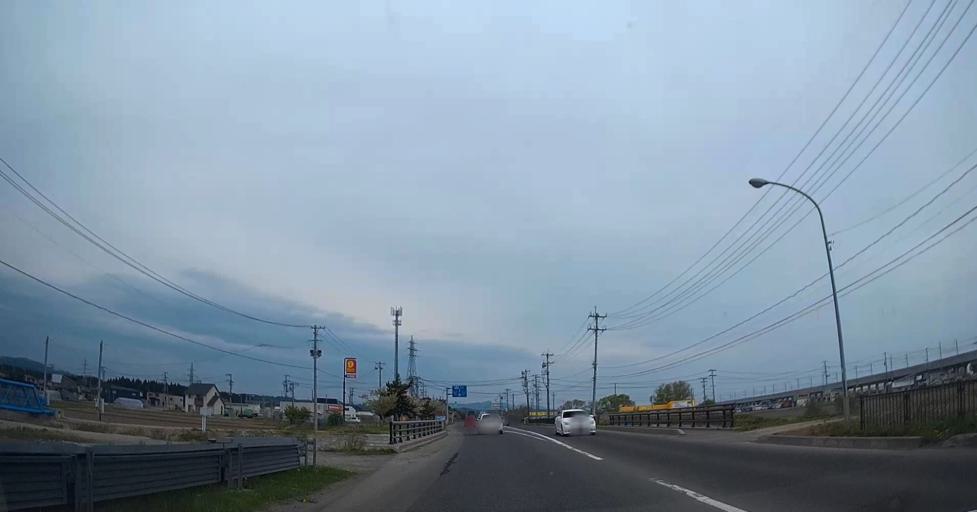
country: JP
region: Aomori
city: Aomori Shi
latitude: 40.8424
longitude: 140.6886
